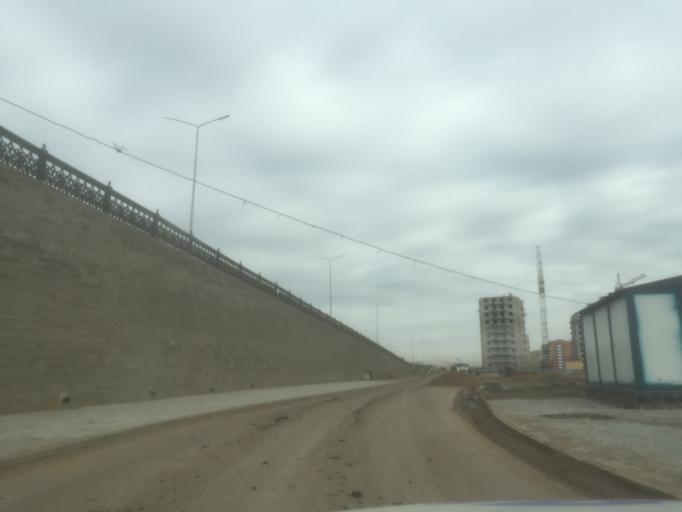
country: KZ
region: Astana Qalasy
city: Astana
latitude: 51.1654
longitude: 71.3755
